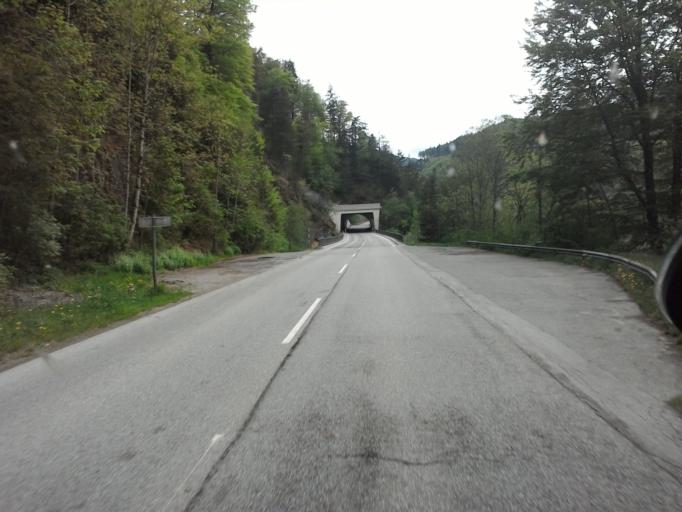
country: AT
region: Styria
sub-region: Politischer Bezirk Liezen
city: Altenmarkt bei Sankt Gallen
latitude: 47.7023
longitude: 14.6884
